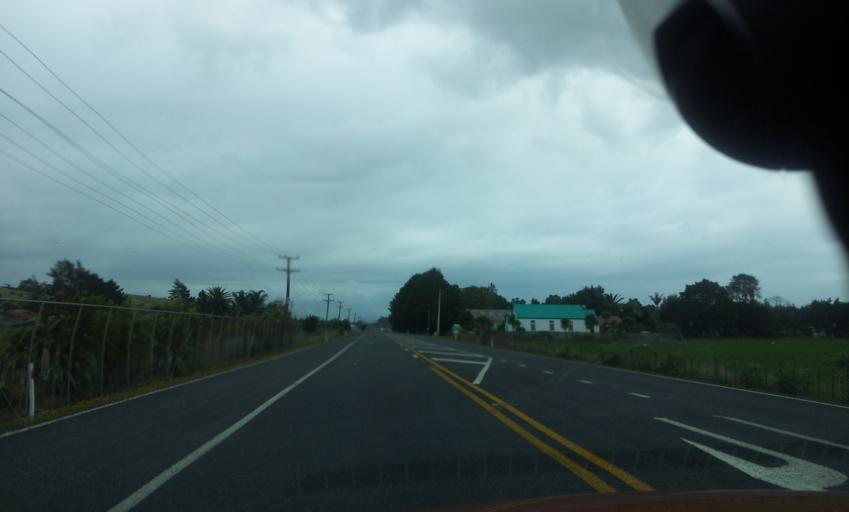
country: NZ
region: Northland
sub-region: Whangarei
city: Ruakaka
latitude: -35.8986
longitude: 174.4420
